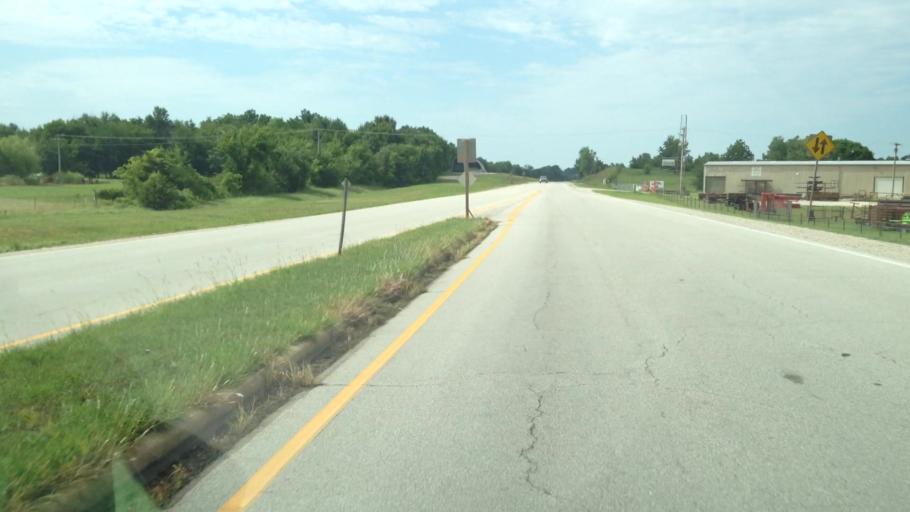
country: US
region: Kansas
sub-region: Labette County
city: Chetopa
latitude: 37.0491
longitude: -95.1007
